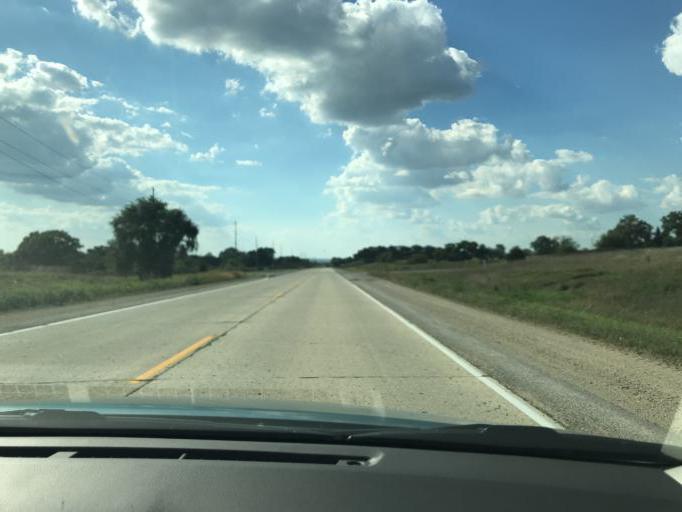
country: US
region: Wisconsin
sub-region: Rock County
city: Orfordville
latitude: 42.5580
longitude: -89.3055
